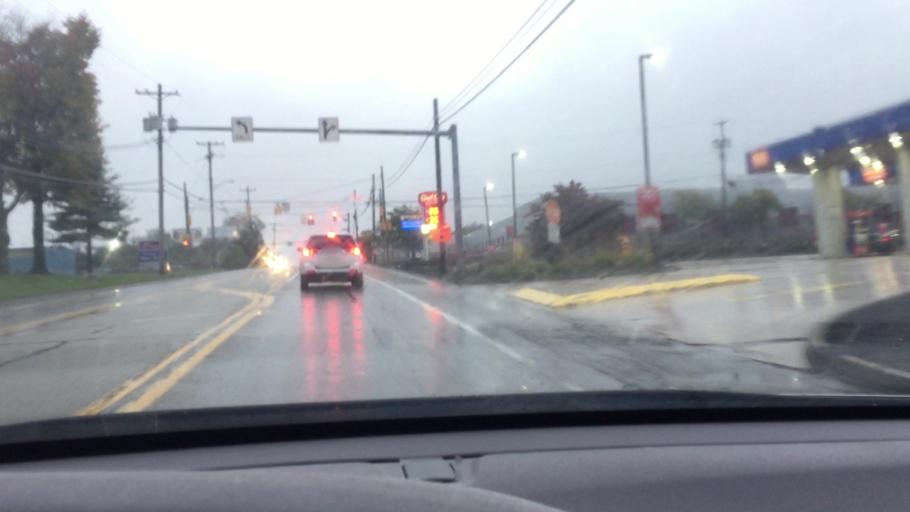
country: US
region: Pennsylvania
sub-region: Allegheny County
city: Pleasant Hills
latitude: 40.3613
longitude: -79.9326
